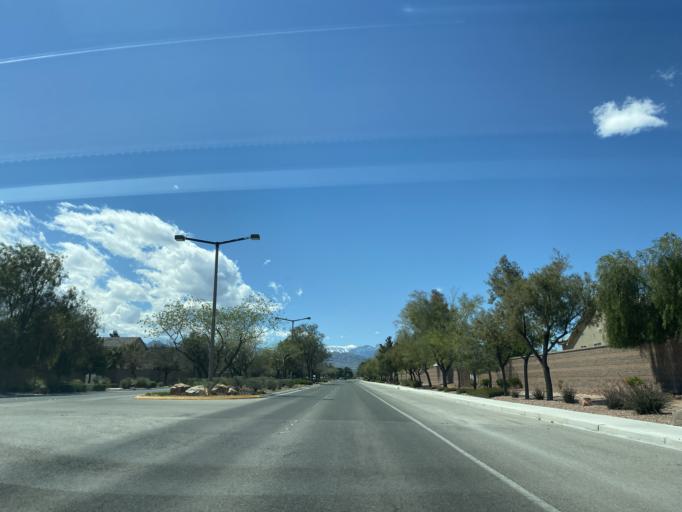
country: US
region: Nevada
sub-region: Clark County
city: North Las Vegas
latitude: 36.3053
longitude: -115.2195
